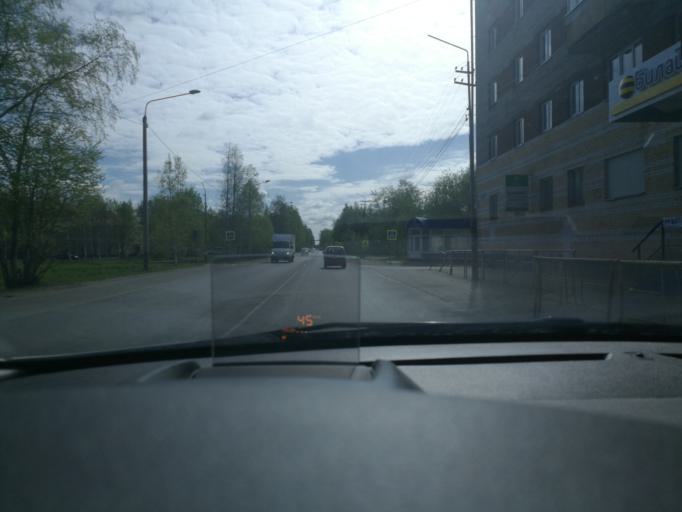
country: RU
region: Arkhangelskaya
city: Arkhangel'sk
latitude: 64.5940
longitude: 40.5815
